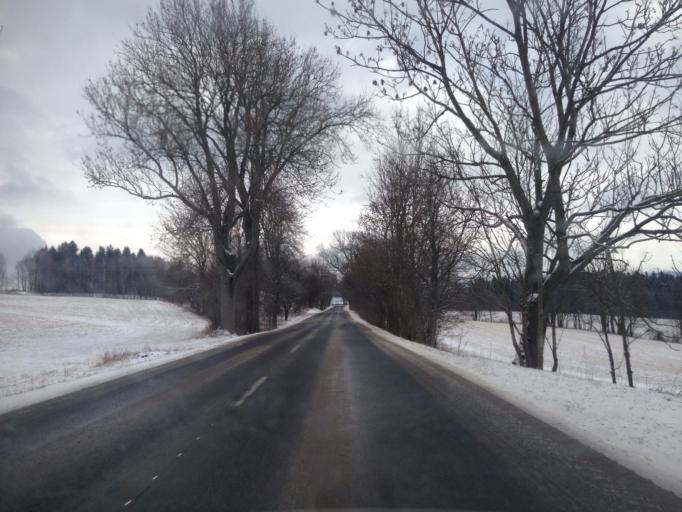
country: CZ
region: Liberecky
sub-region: Okres Semily
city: Vysoke nad Jizerou
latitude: 50.6723
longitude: 15.4091
